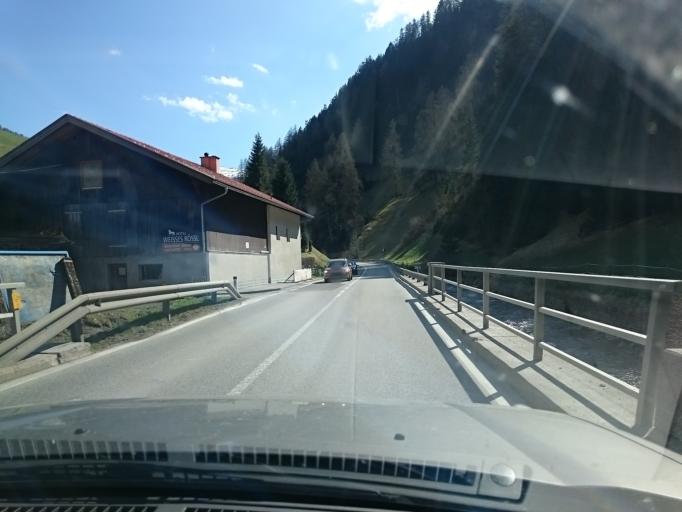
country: AT
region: Tyrol
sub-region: Politischer Bezirk Innsbruck Land
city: Gries am Brenner
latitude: 47.0562
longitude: 11.4851
